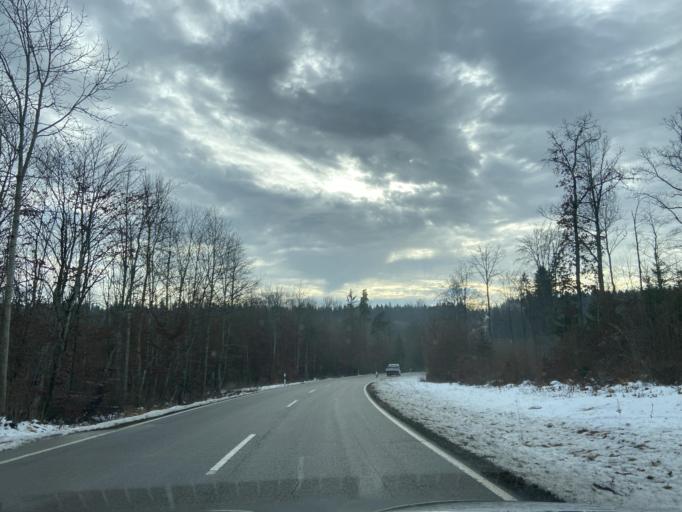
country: DE
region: Baden-Wuerttemberg
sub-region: Tuebingen Region
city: Bingen
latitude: 48.1493
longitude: 9.2597
